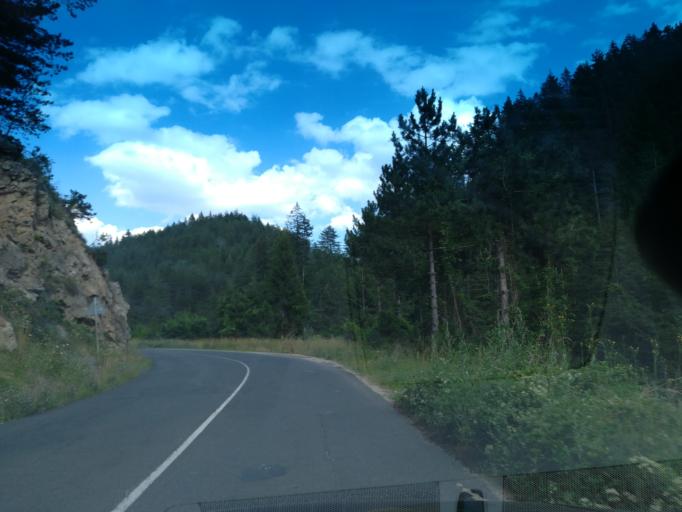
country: BG
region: Smolyan
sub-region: Obshtina Smolyan
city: Smolyan
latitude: 41.6484
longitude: 24.7677
